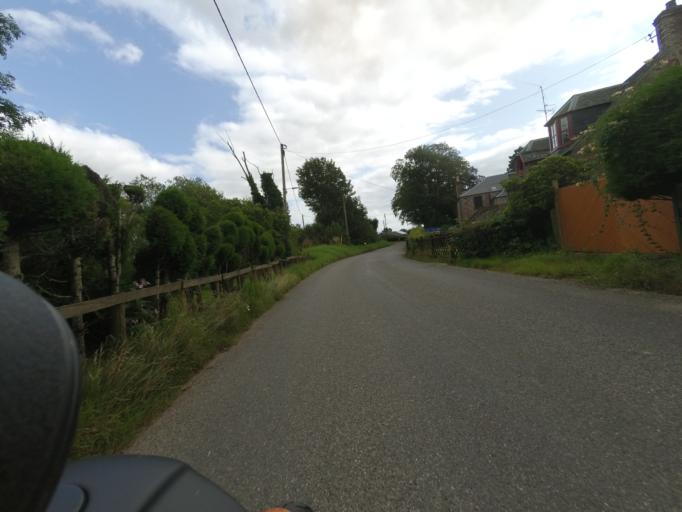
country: GB
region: Scotland
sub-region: Aberdeenshire
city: Laurencekirk
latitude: 56.8477
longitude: -2.5695
